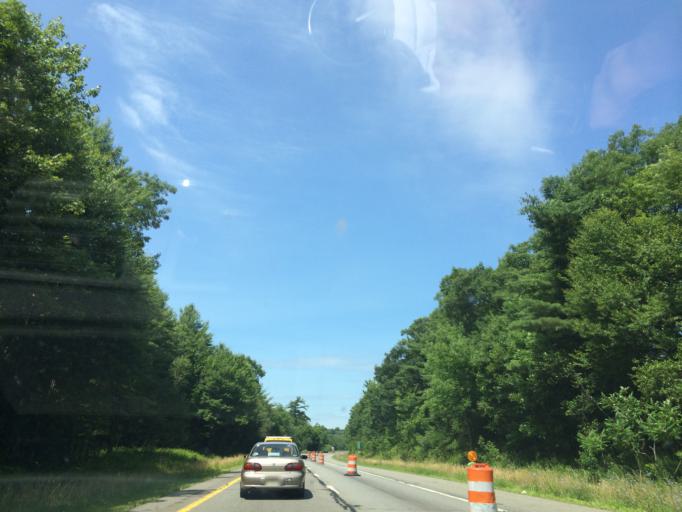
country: US
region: Pennsylvania
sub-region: Pike County
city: Gold Key Lake
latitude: 41.3421
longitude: -74.9139
